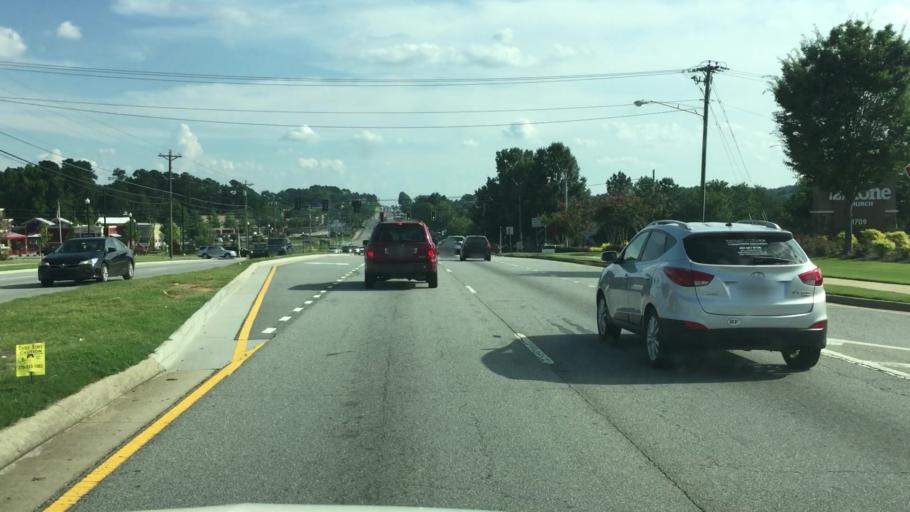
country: US
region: Georgia
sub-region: Gwinnett County
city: Snellville
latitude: 33.8810
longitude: -84.0117
